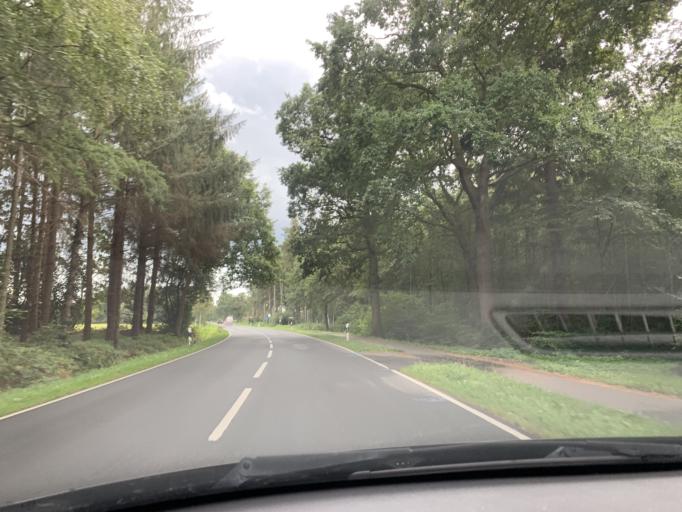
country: DE
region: Lower Saxony
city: Westerstede
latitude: 53.3010
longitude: 7.9159
